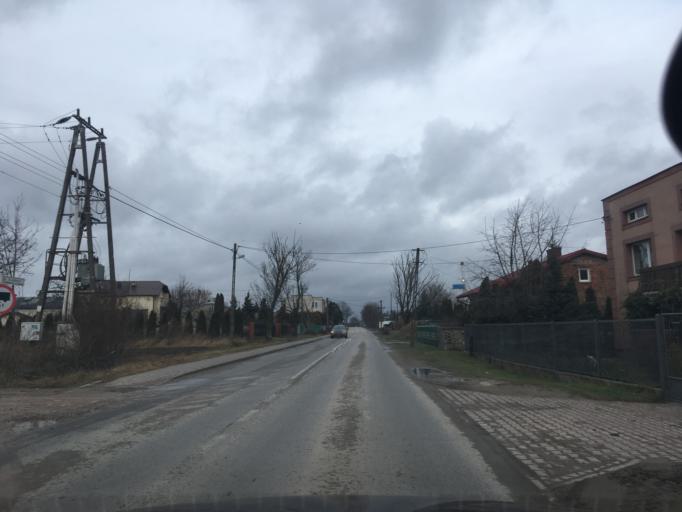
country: PL
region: Masovian Voivodeship
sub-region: Powiat piaseczynski
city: Lesznowola
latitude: 52.1106
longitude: 20.9315
